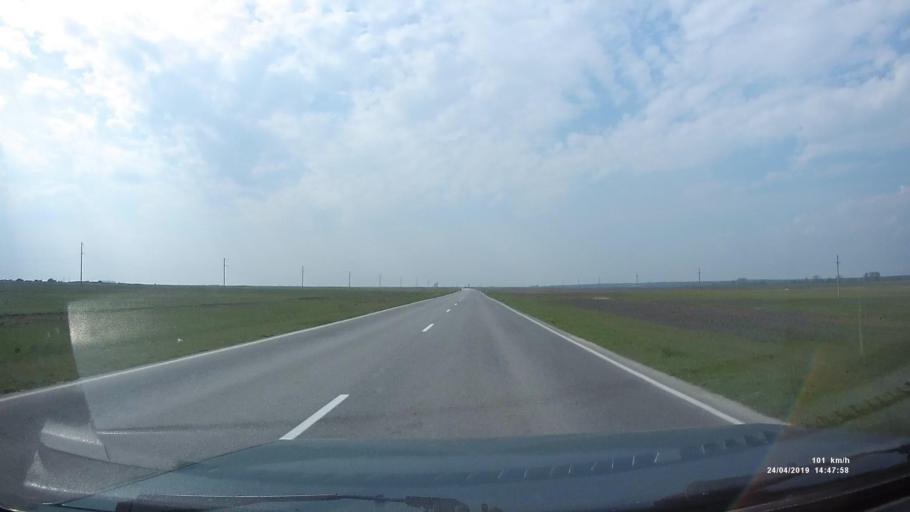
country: RU
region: Rostov
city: Remontnoye
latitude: 46.4965
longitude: 43.7638
